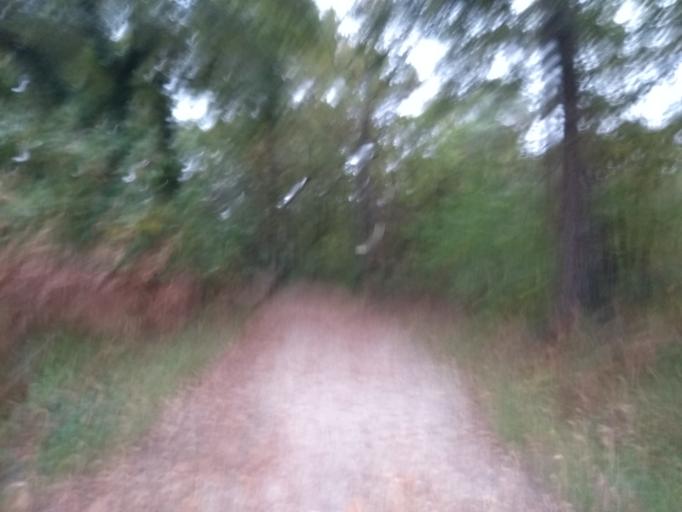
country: FR
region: Aquitaine
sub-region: Departement de la Gironde
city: Talence
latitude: 44.7937
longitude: -0.5944
